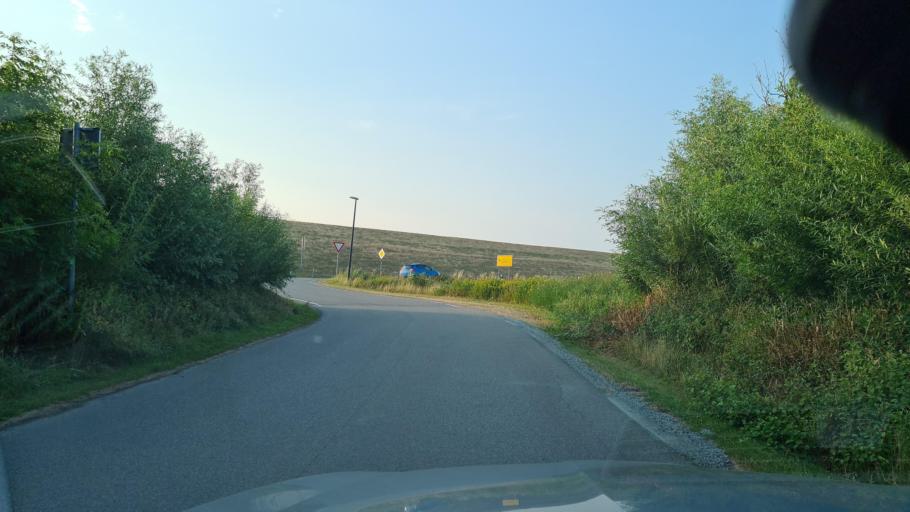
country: DE
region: Schleswig-Holstein
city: Elisabeth-Sophien-Koog
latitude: 54.4996
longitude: 8.8113
